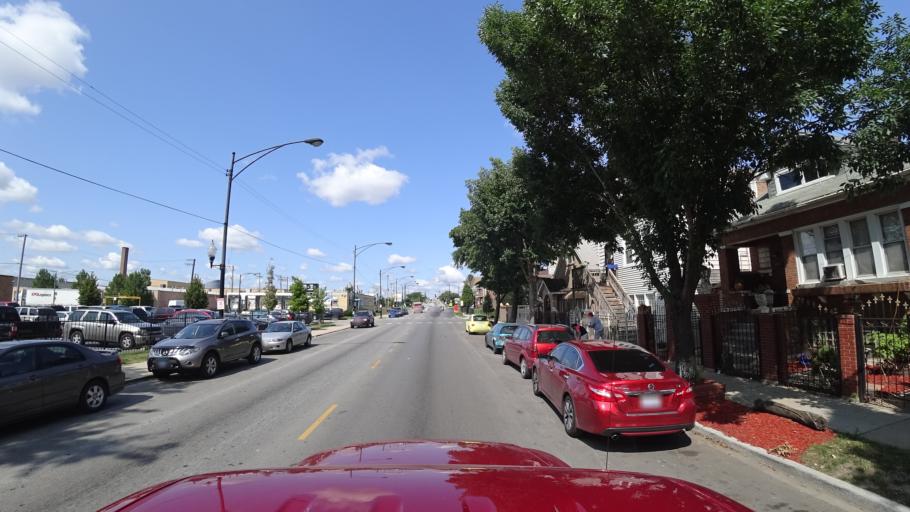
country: US
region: Illinois
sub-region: Cook County
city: Cicero
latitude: 41.8368
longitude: -87.7322
